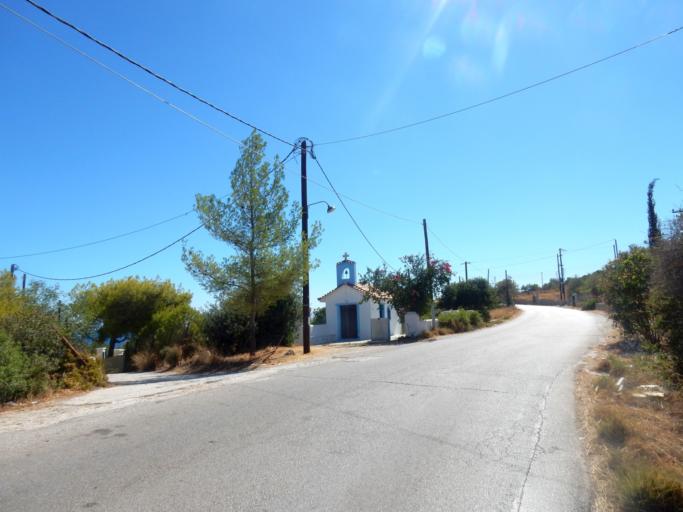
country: GR
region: Attica
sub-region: Nomos Piraios
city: Vathi
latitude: 37.7702
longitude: 23.4740
